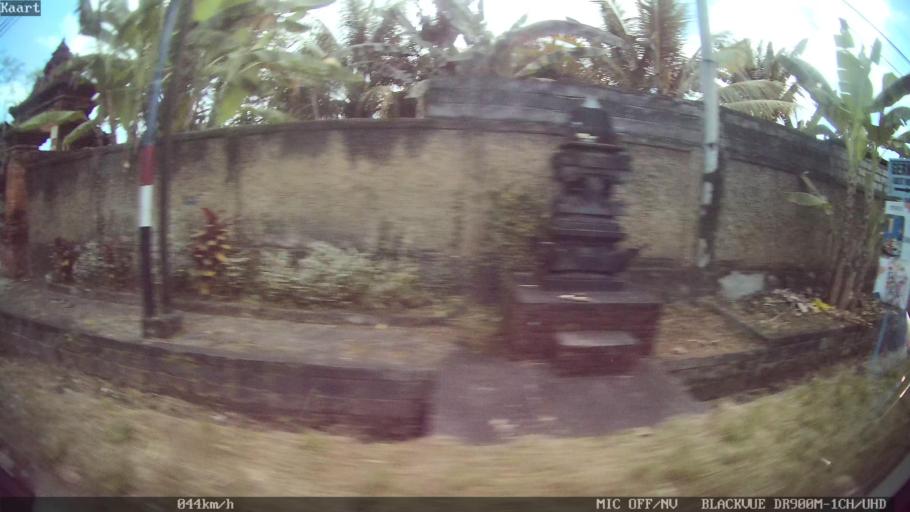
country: ID
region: Bali
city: Banjar Sedang
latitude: -8.5635
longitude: 115.2862
